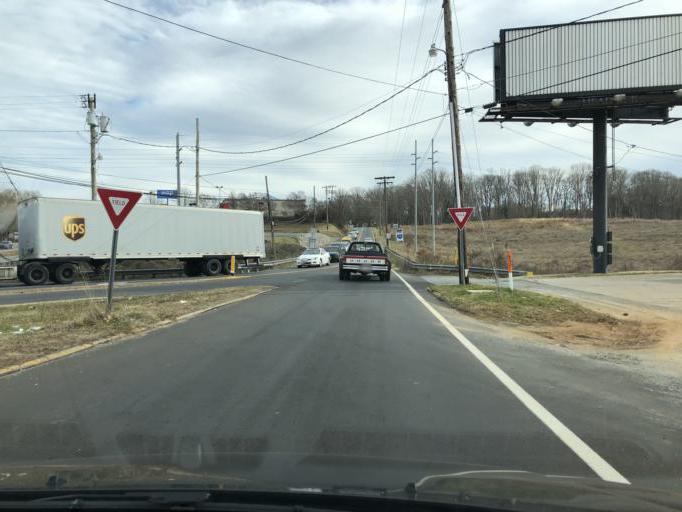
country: US
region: North Carolina
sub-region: Cleveland County
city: Shelby
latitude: 35.2754
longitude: -81.5329
